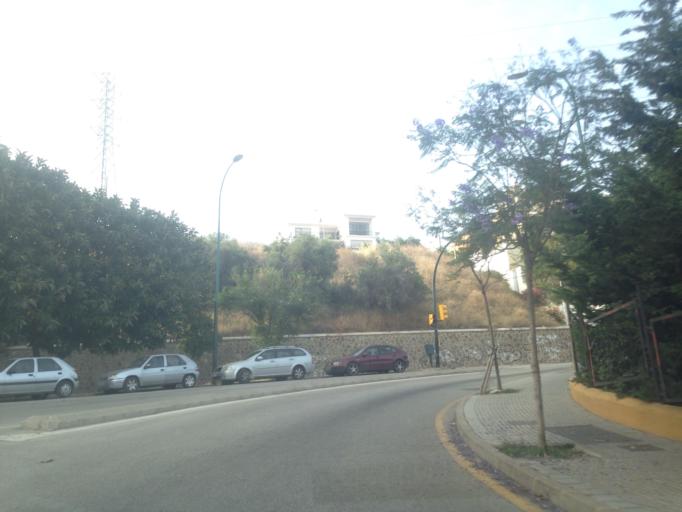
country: ES
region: Andalusia
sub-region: Provincia de Malaga
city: Malaga
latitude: 36.7361
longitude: -4.4159
